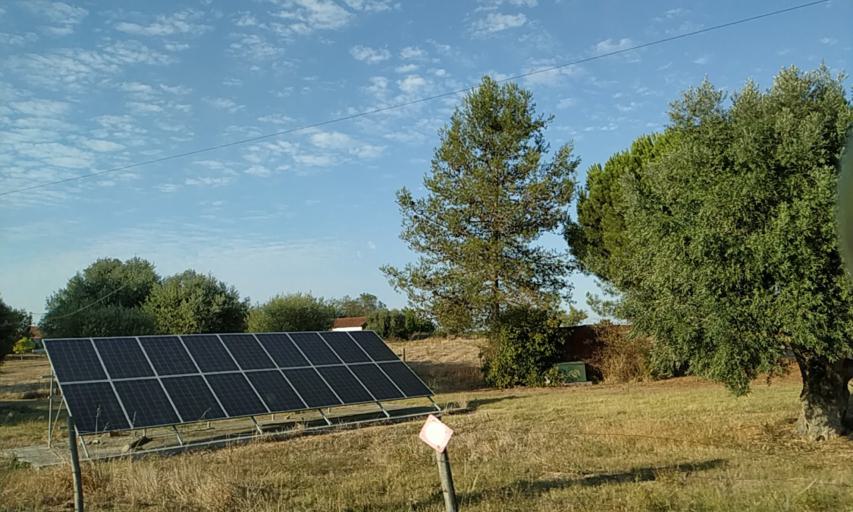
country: PT
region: Santarem
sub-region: Santarem
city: Santarem
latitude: 39.3341
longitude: -8.6605
